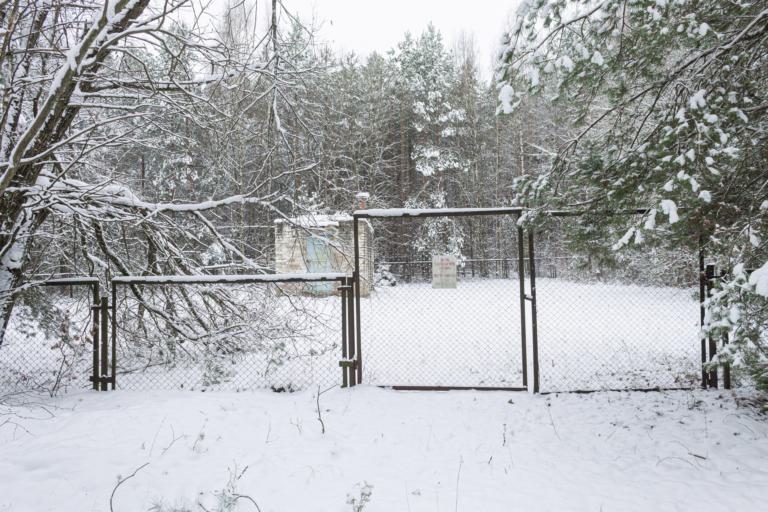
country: BY
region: Brest
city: Kamyanyets
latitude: 52.3789
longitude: 23.8660
